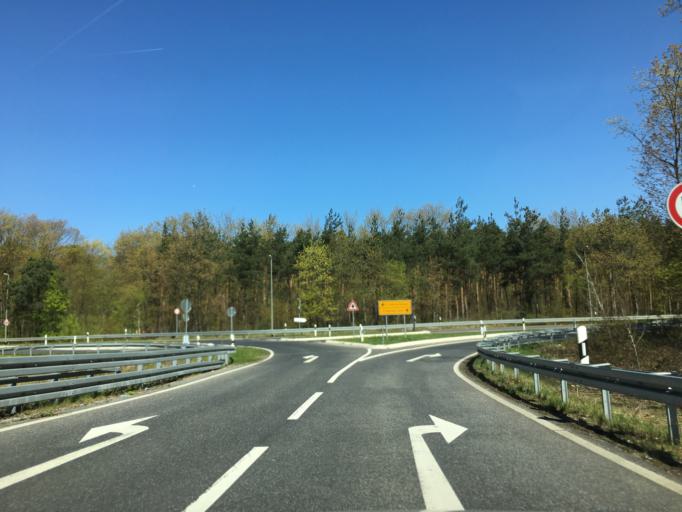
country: DE
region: Hesse
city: Niederrad
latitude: 50.0584
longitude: 8.5910
